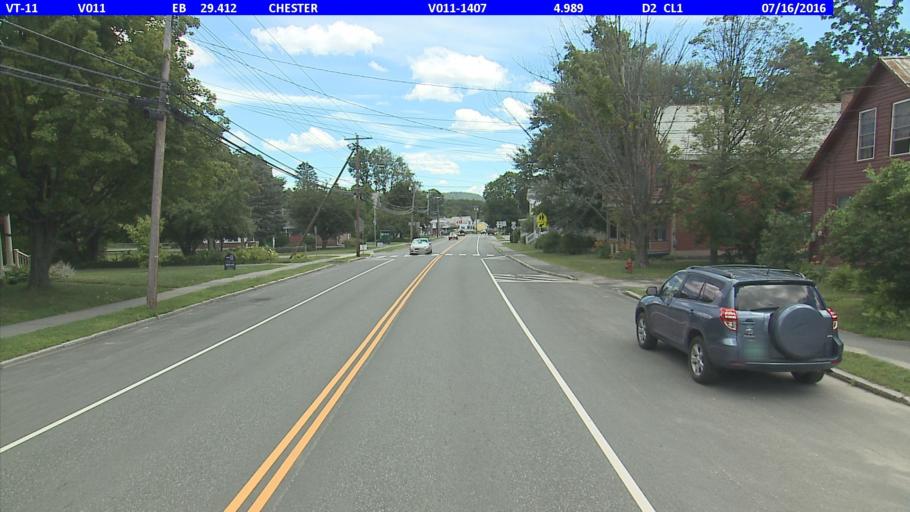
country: US
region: Vermont
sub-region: Windsor County
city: Chester
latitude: 43.2638
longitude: -72.5969
